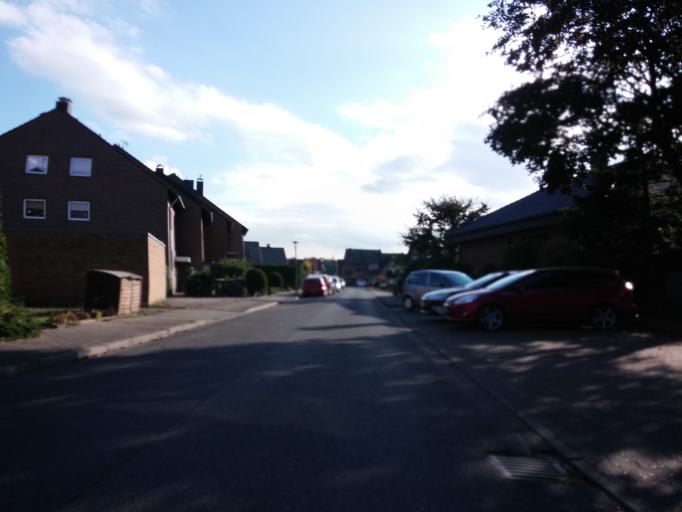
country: DE
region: North Rhine-Westphalia
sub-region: Regierungsbezirk Munster
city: Gladbeck
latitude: 51.6113
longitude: 6.9678
